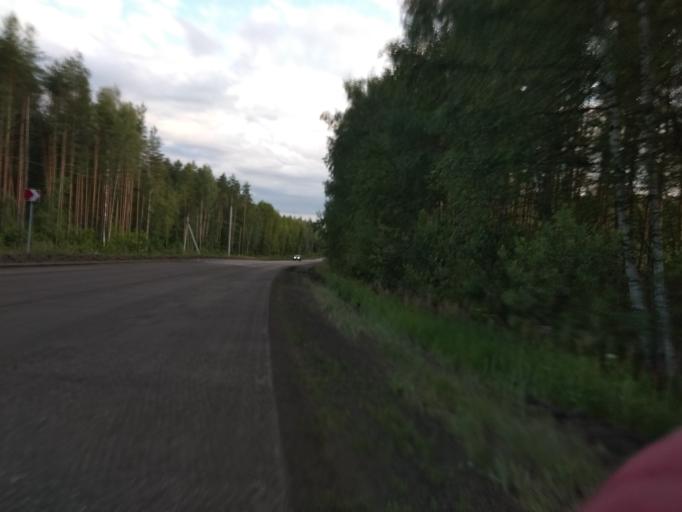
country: RU
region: Moskovskaya
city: Misheronskiy
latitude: 55.6441
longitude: 39.7567
